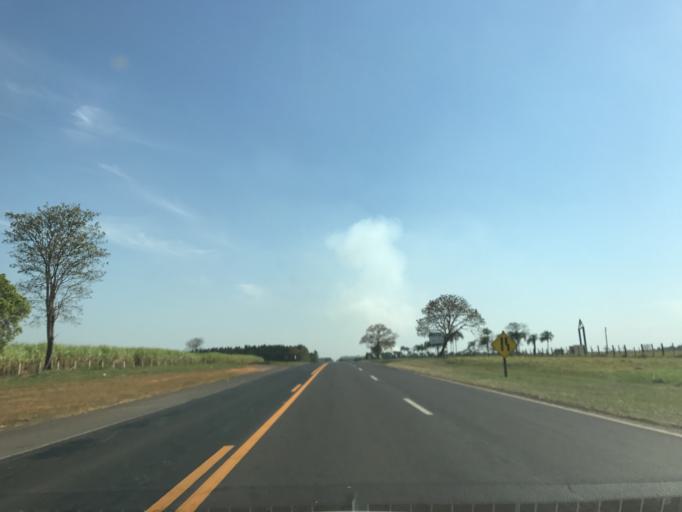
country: BR
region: Sao Paulo
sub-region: Penapolis
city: Penapolis
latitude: -21.3555
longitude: -50.0624
